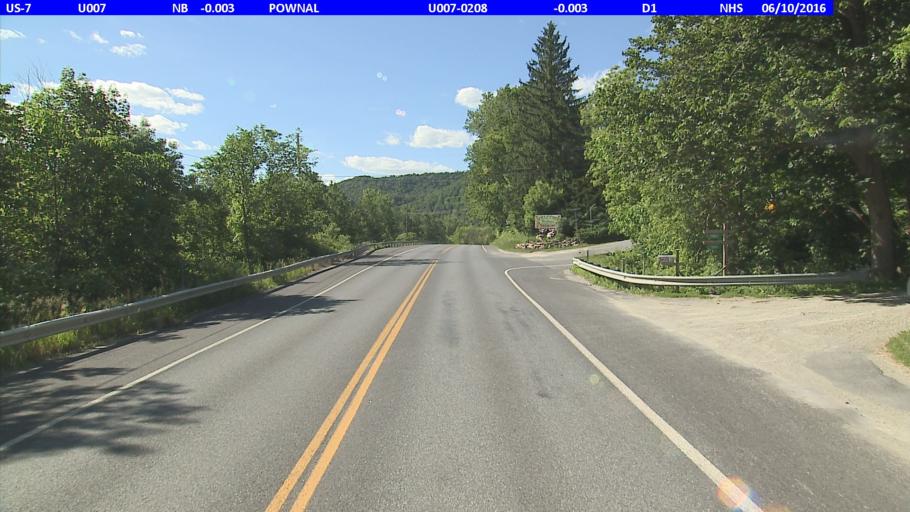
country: US
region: Massachusetts
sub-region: Berkshire County
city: Williamstown
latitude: 42.7449
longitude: -73.2132
